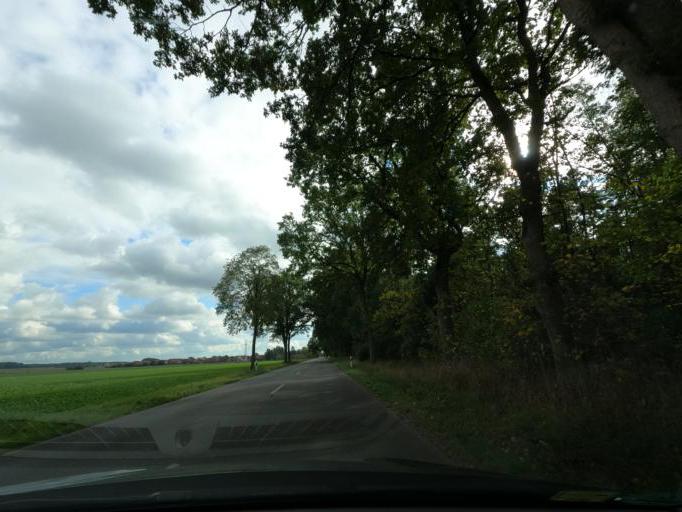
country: DE
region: Lower Saxony
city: Klein Schwulper
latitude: 52.3641
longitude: 10.4275
